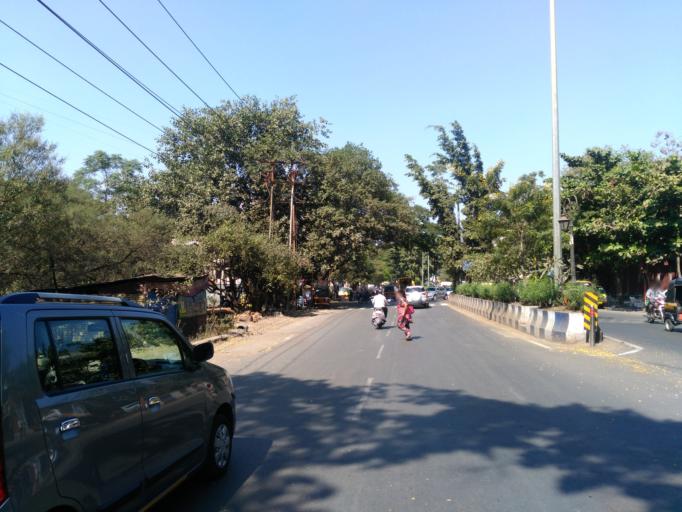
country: IN
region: Maharashtra
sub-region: Pune Division
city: Pune
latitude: 18.4747
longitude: 73.8624
